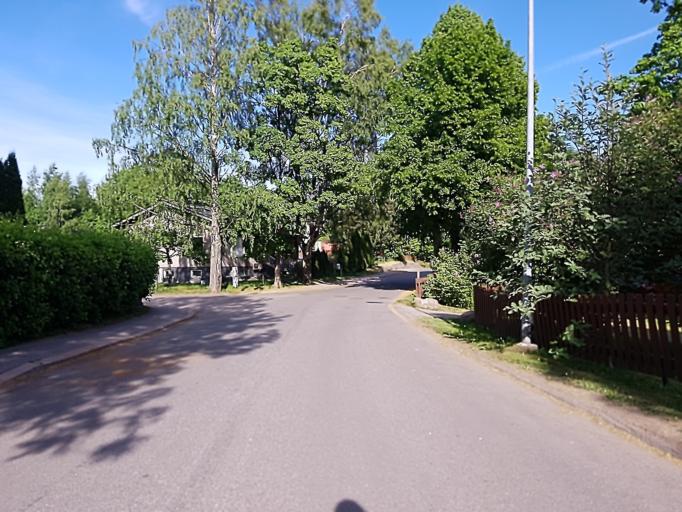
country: FI
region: Uusimaa
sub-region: Helsinki
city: Helsinki
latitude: 60.2438
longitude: 24.9529
